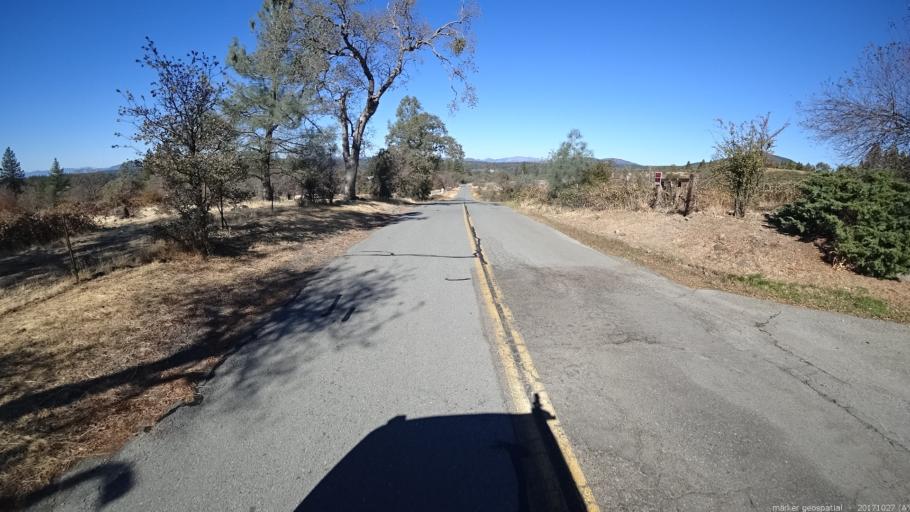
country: US
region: California
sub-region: Shasta County
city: Shingletown
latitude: 40.7607
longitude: -121.9689
